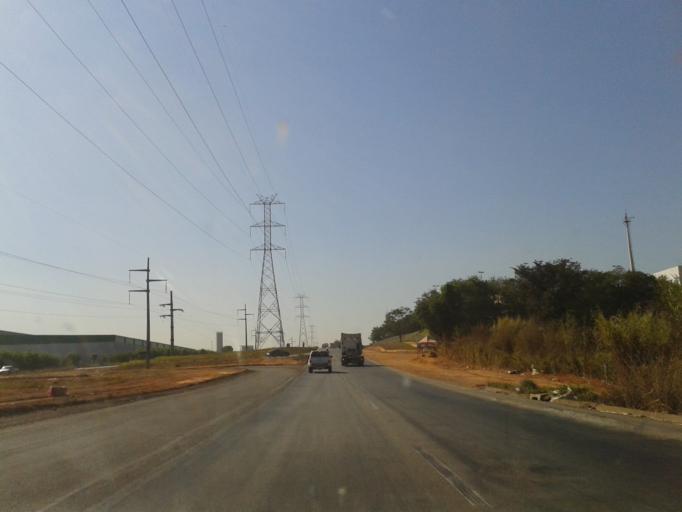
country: BR
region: Goias
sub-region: Aparecida De Goiania
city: Aparecida de Goiania
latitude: -16.7861
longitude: -49.2584
